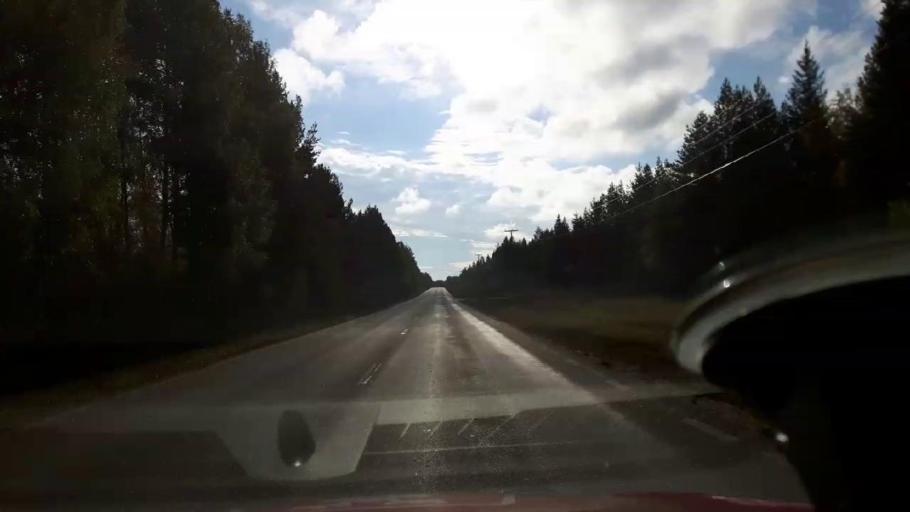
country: SE
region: Jaemtland
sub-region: Harjedalens Kommun
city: Sveg
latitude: 62.0982
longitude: 15.0775
